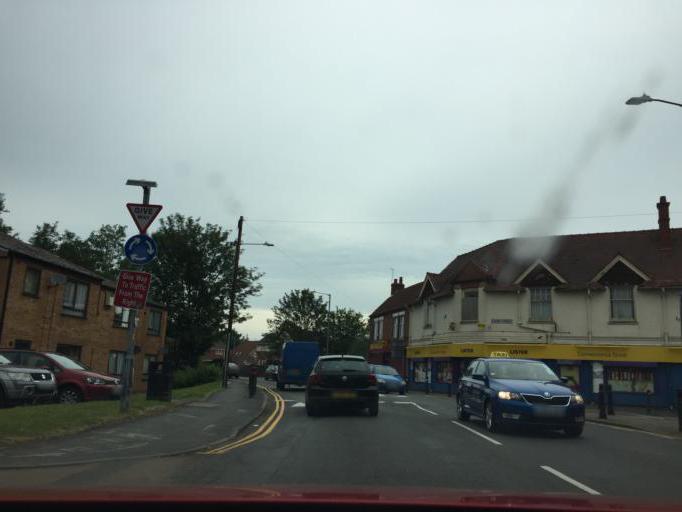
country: GB
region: England
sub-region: Warwickshire
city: Attleborough
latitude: 52.5180
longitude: -1.4590
